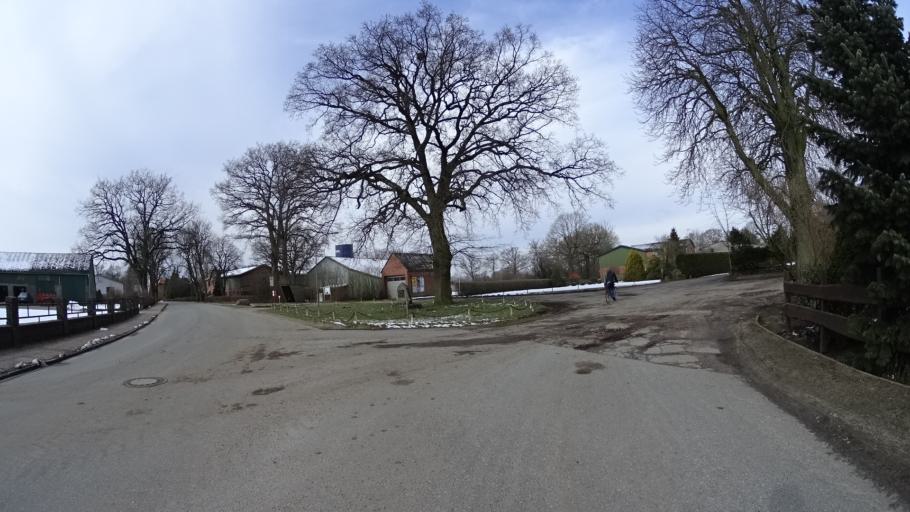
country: DE
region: Schleswig-Holstein
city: Gross Kummerfeld
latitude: 54.0287
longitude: 10.1162
